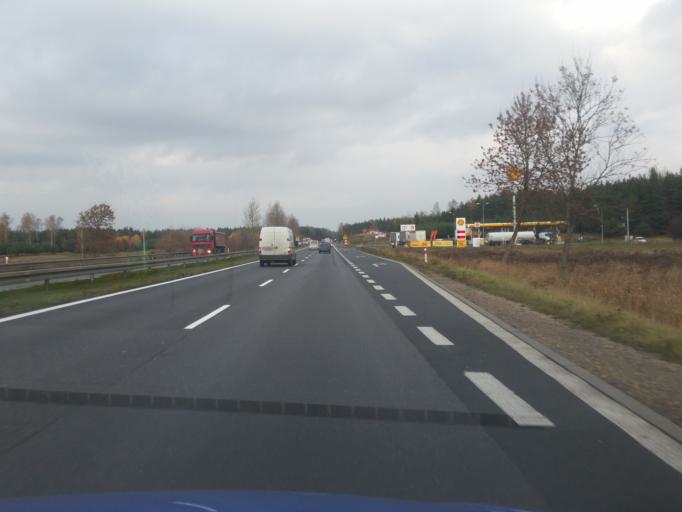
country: PL
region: Silesian Voivodeship
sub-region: Powiat bedzinski
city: Siewierz
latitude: 50.5108
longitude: 19.1959
